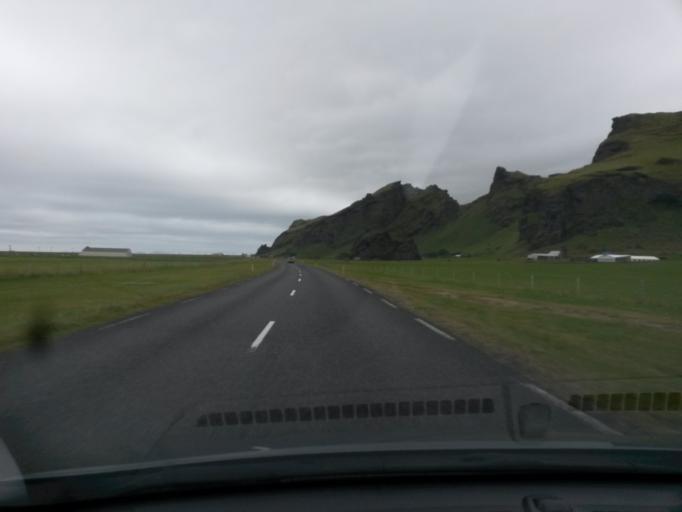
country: IS
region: South
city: Vestmannaeyjar
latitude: 63.5235
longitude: -19.5427
